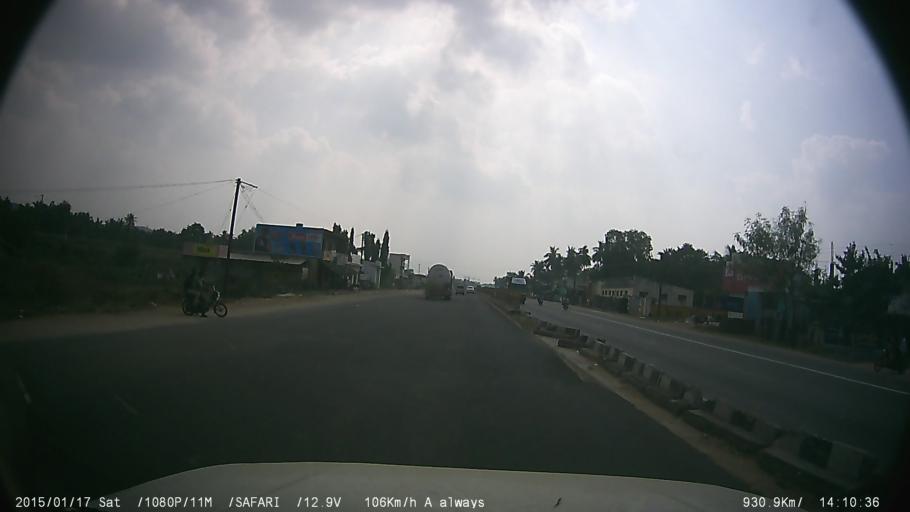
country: IN
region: Tamil Nadu
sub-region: Vellore
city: Ambur
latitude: 12.8029
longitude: 78.7359
